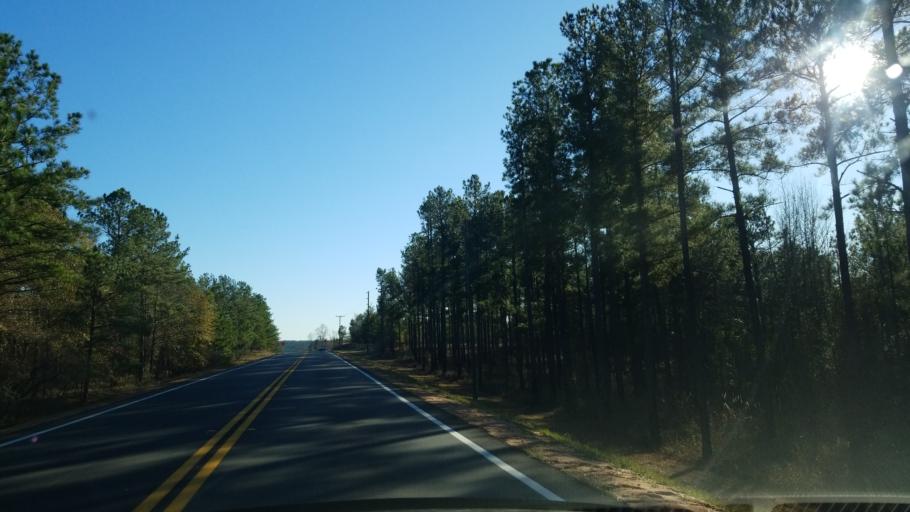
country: US
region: Georgia
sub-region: Talbot County
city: Talbotton
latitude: 32.5705
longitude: -84.5419
